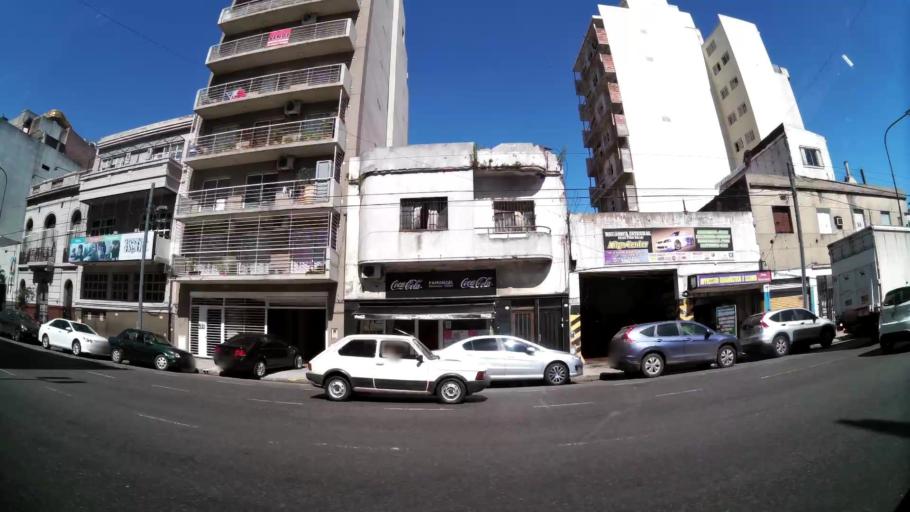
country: AR
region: Buenos Aires F.D.
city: Buenos Aires
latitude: -34.6276
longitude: -58.3911
